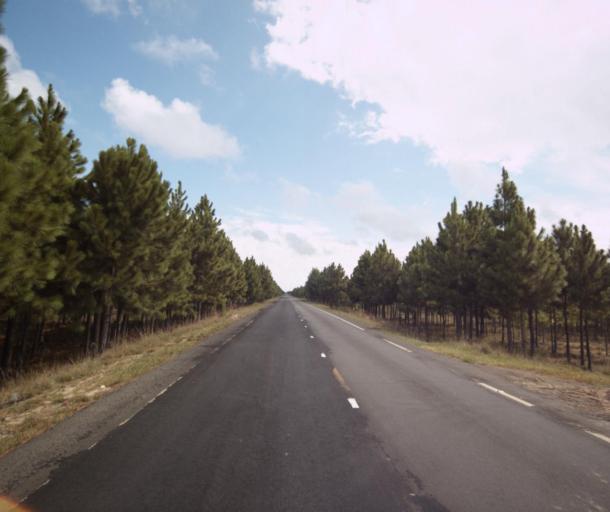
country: BR
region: Rio Grande do Sul
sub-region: Tapes
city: Tapes
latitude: -31.4144
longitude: -51.1724
